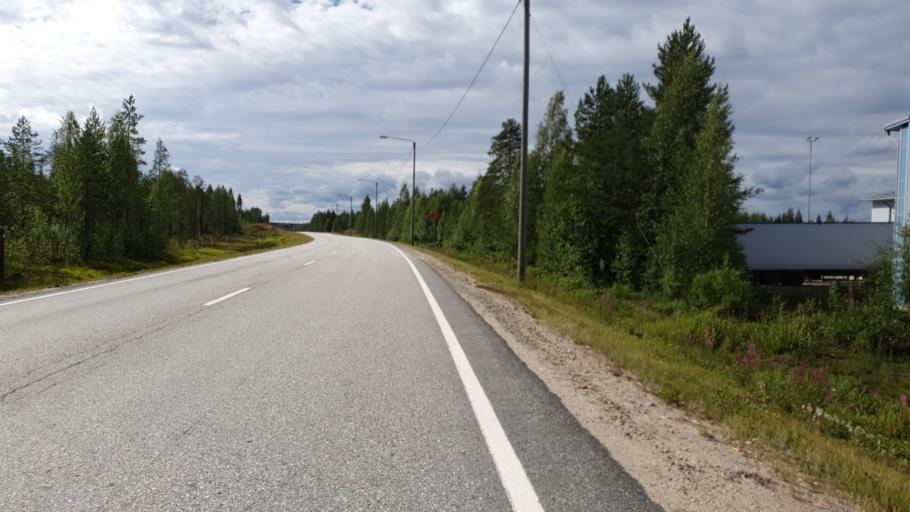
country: FI
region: Kainuu
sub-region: Kehys-Kainuu
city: Kuhmo
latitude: 64.5352
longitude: 29.9441
